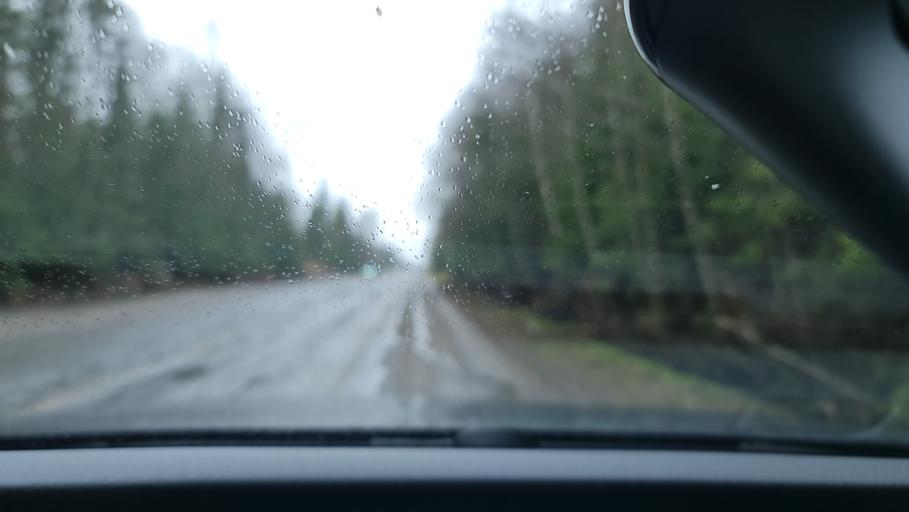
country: RU
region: Novgorod
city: Valday
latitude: 58.0352
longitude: 32.8578
